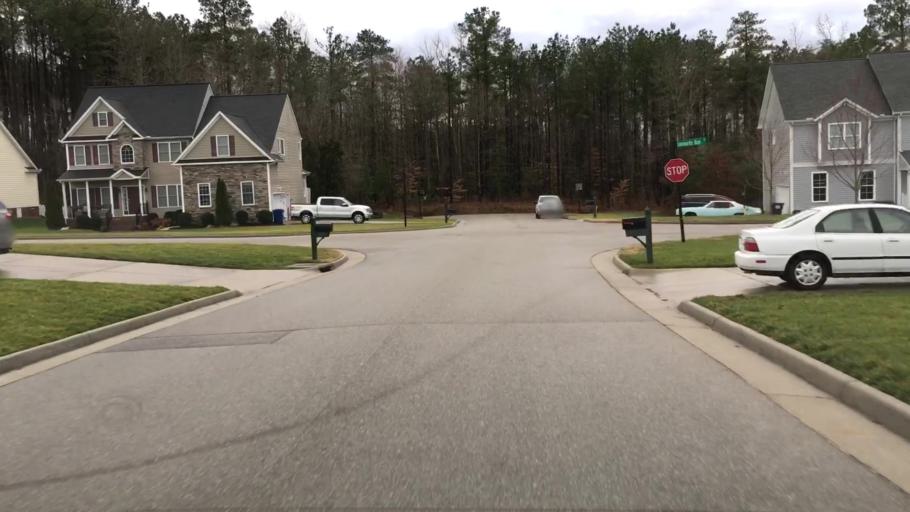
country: US
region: Virginia
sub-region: Chesterfield County
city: Bon Air
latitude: 37.4874
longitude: -77.6038
